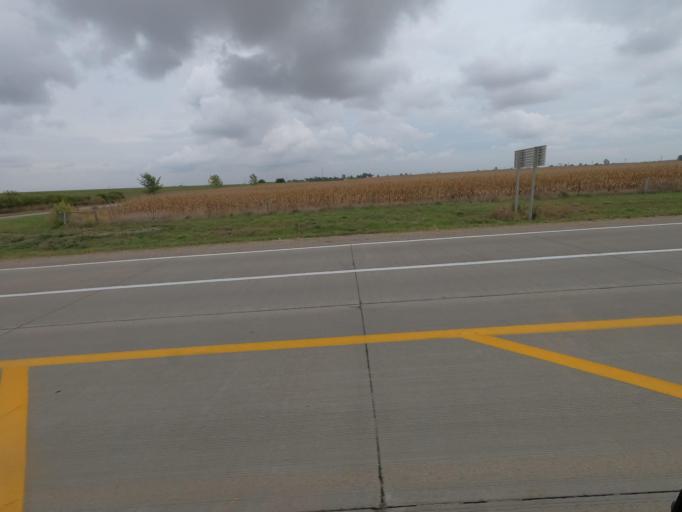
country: US
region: Iowa
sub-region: Wapello County
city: Ottumwa
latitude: 40.9966
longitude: -92.2369
